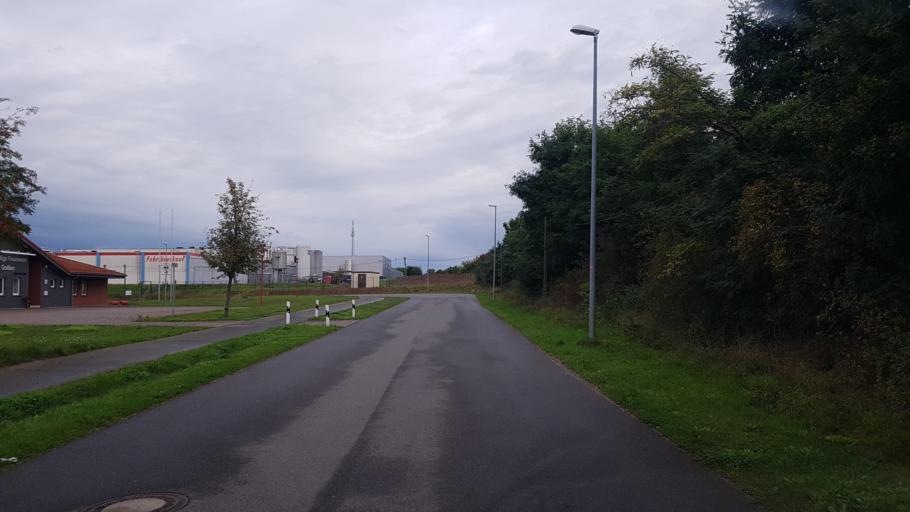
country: DE
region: Brandenburg
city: Golssen
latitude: 51.9733
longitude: 13.5785
